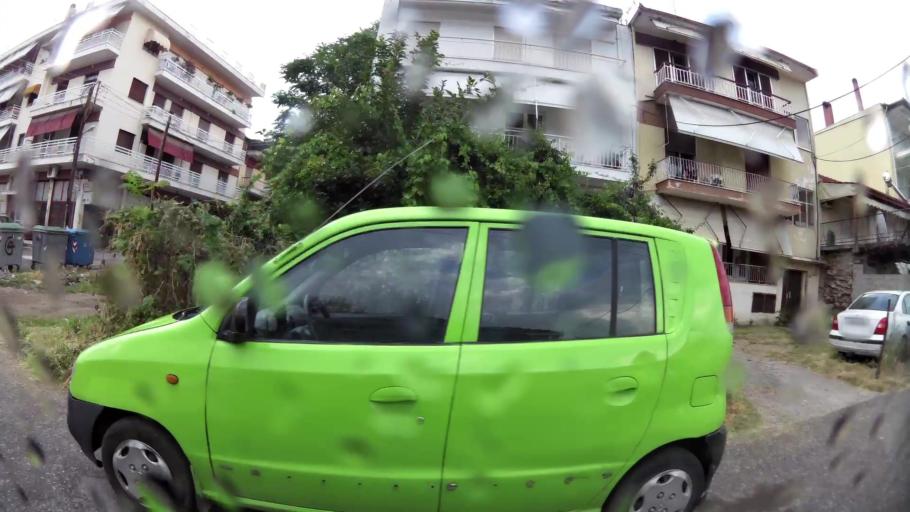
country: GR
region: Central Macedonia
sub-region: Nomos Imathias
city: Veroia
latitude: 40.5273
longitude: 22.2002
